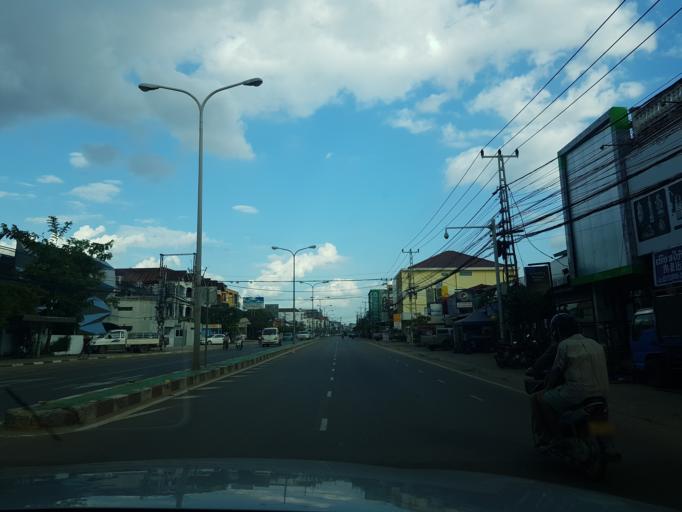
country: TH
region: Nong Khai
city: Si Chiang Mai
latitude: 17.9694
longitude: 102.5816
